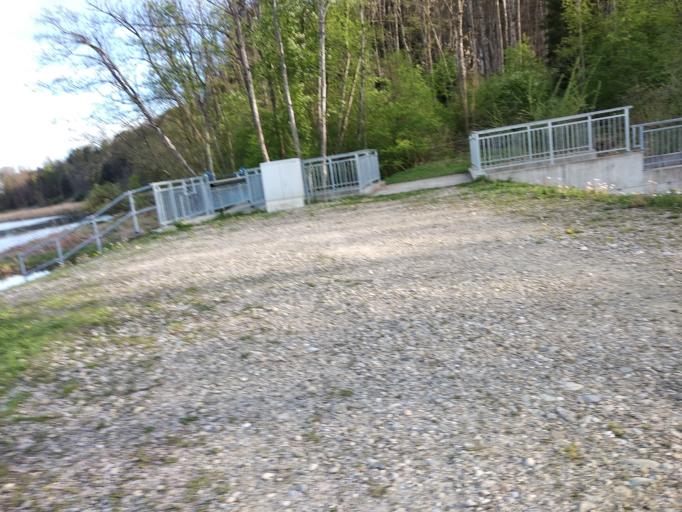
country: DE
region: Bavaria
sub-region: Swabia
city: Kronburg
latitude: 47.8903
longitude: 10.1450
